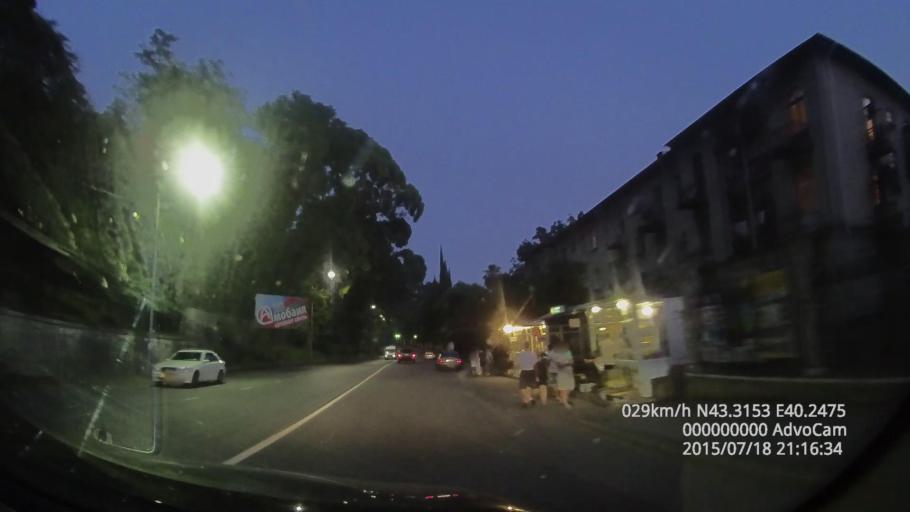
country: GE
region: Abkhazia
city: Gagra
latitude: 43.3152
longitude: 40.2476
